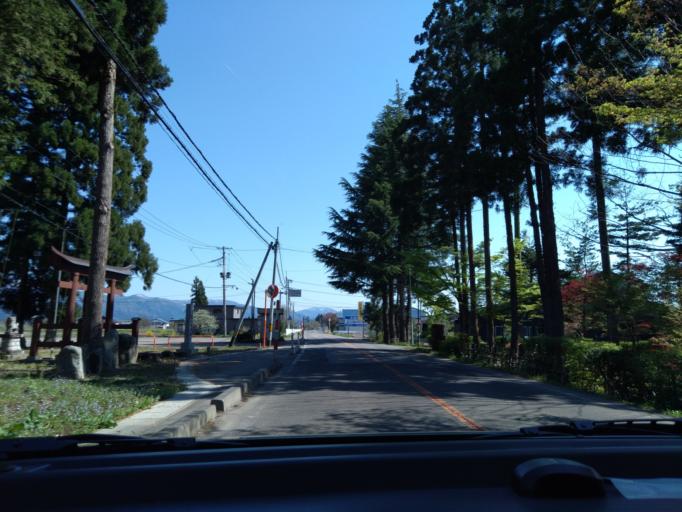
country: JP
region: Akita
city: Kakunodatemachi
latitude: 39.5284
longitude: 140.5864
